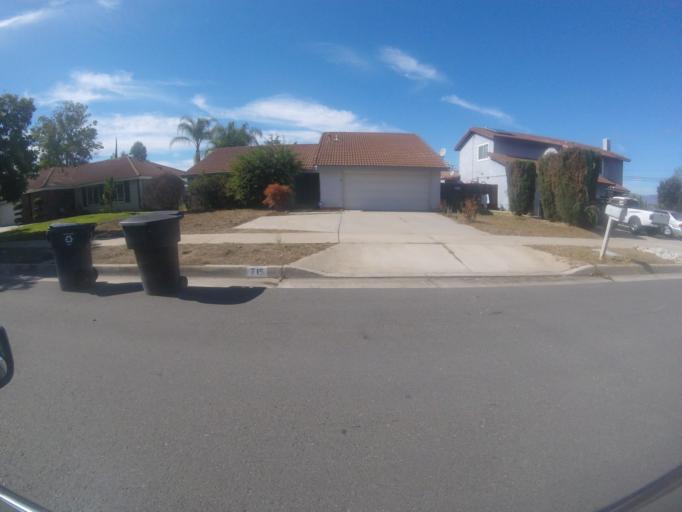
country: US
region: California
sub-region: San Bernardino County
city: Mentone
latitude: 34.0624
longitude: -117.1476
